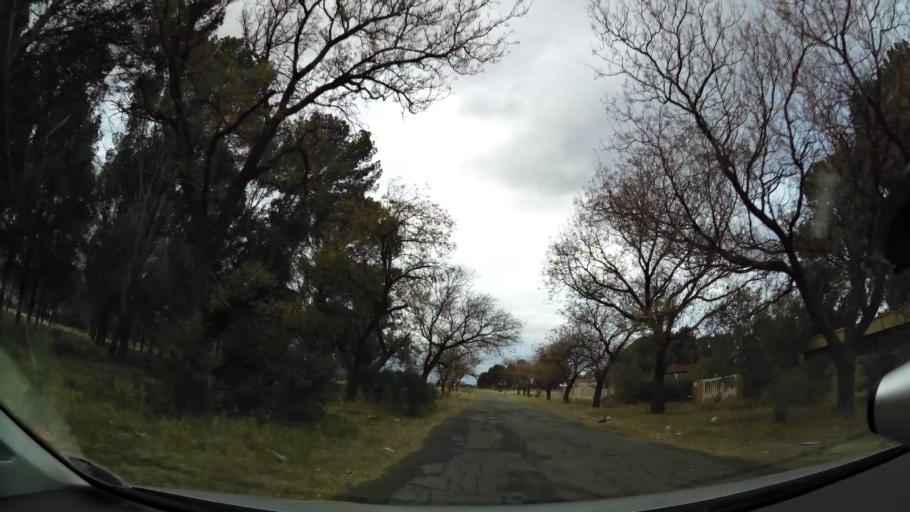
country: ZA
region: Orange Free State
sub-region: Lejweleputswa District Municipality
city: Welkom
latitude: -27.9619
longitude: 26.7137
